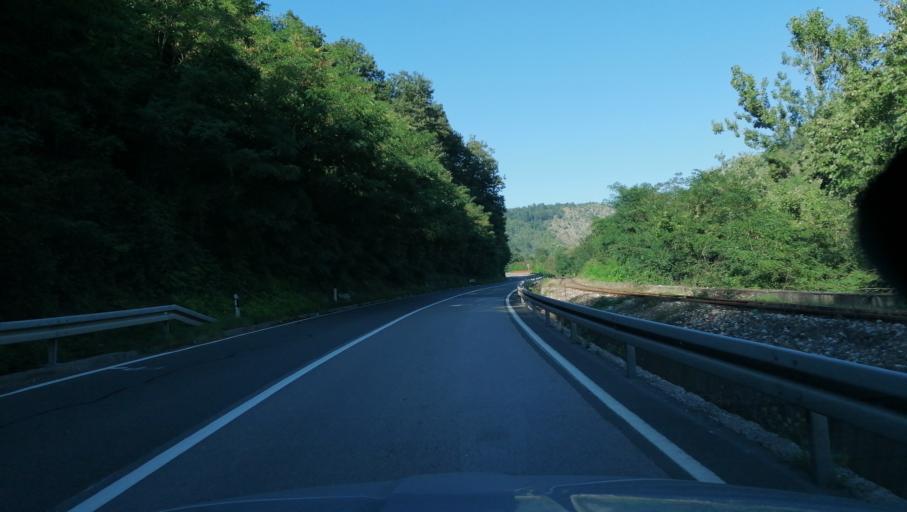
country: RS
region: Central Serbia
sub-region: Raski Okrug
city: Kraljevo
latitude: 43.6594
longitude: 20.5623
